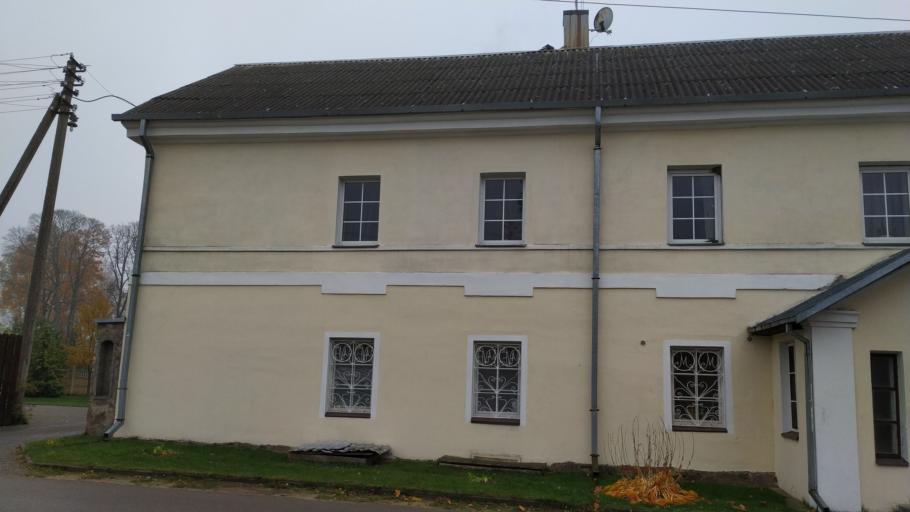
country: BY
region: Grodnenskaya
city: Astravyets
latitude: 54.6093
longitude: 25.7239
